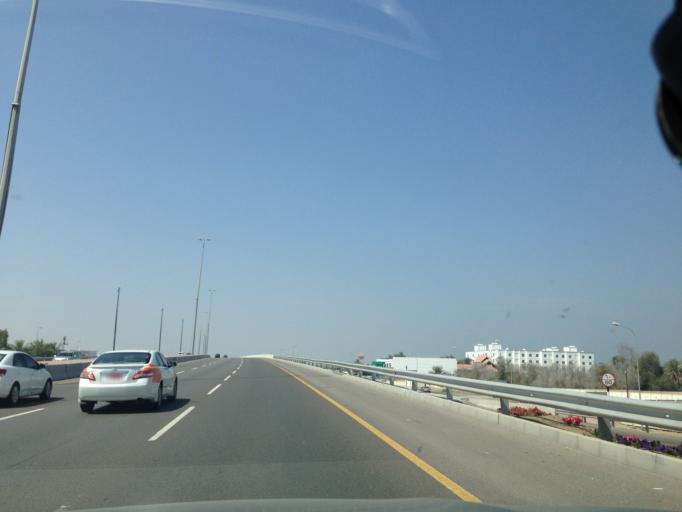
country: OM
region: Muhafazat Masqat
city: As Sib al Jadidah
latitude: 23.6535
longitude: 58.2097
